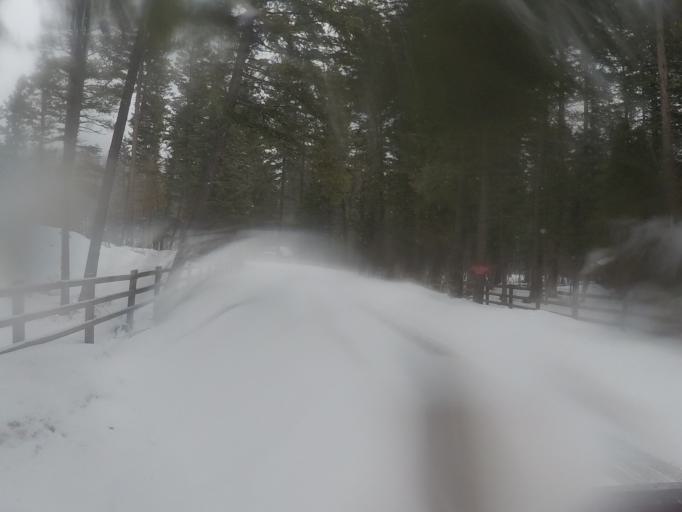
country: US
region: Montana
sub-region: Missoula County
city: Seeley Lake
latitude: 47.4510
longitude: -113.6051
